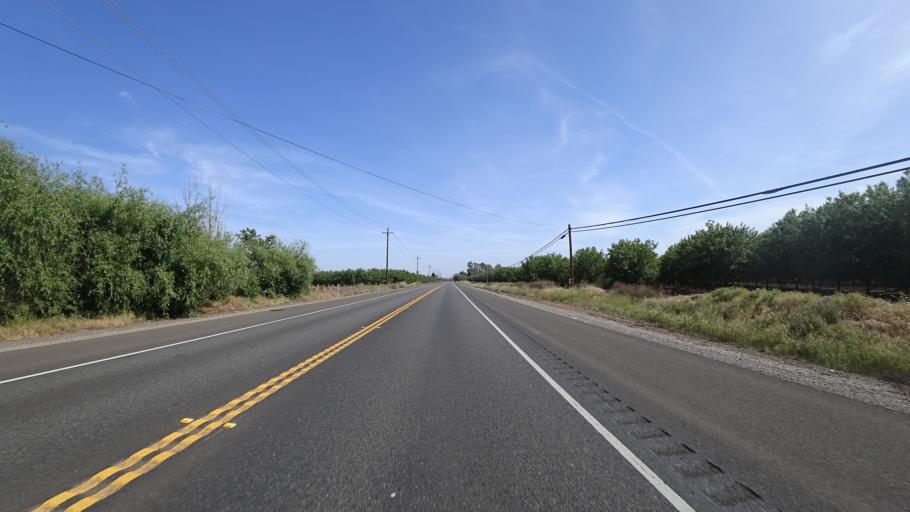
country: US
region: California
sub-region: Butte County
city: Chico
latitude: 39.8029
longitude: -121.9066
